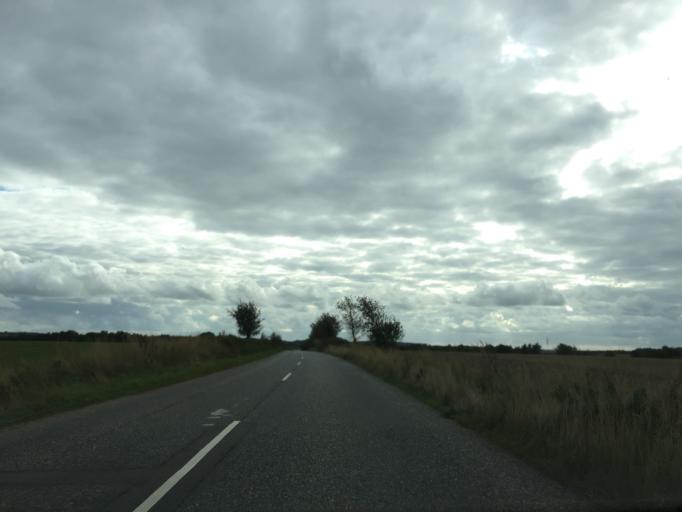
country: DK
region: Central Jutland
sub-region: Favrskov Kommune
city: Hammel
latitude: 56.2419
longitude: 9.7554
